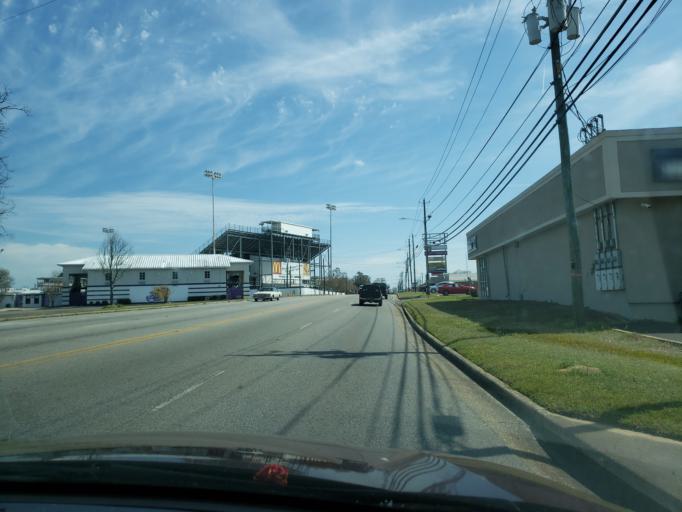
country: US
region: Alabama
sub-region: Elmore County
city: Tallassee
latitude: 32.5428
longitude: -85.9037
